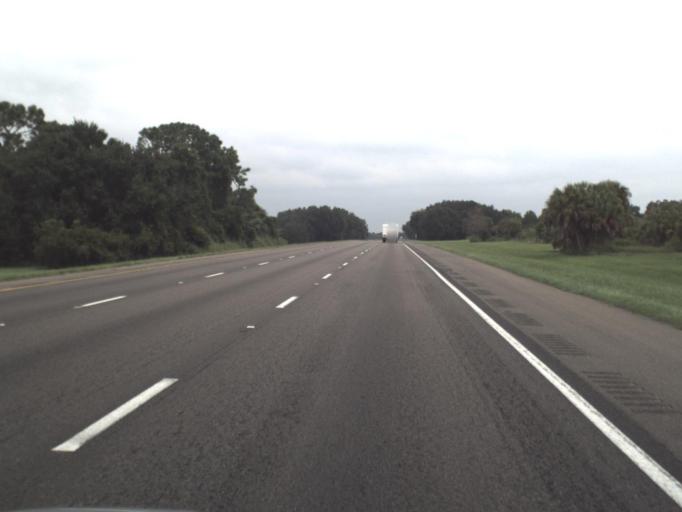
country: US
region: Florida
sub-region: Hillsborough County
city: Ruskin
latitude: 27.6297
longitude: -82.4713
